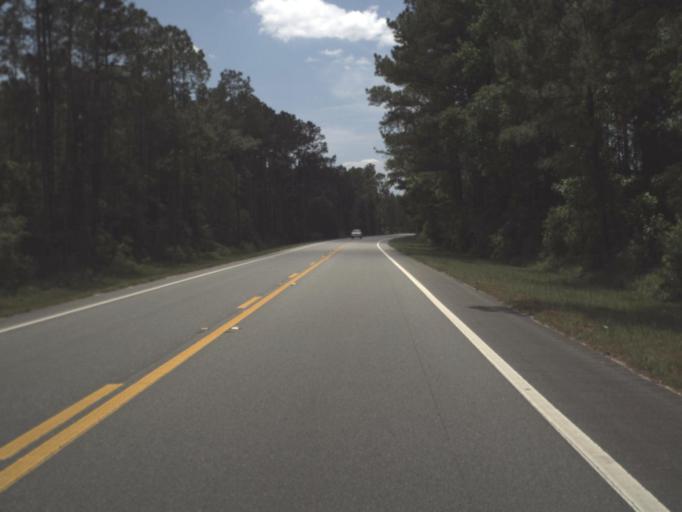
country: US
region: Florida
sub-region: Calhoun County
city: Blountstown
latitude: 30.2982
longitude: -85.1312
